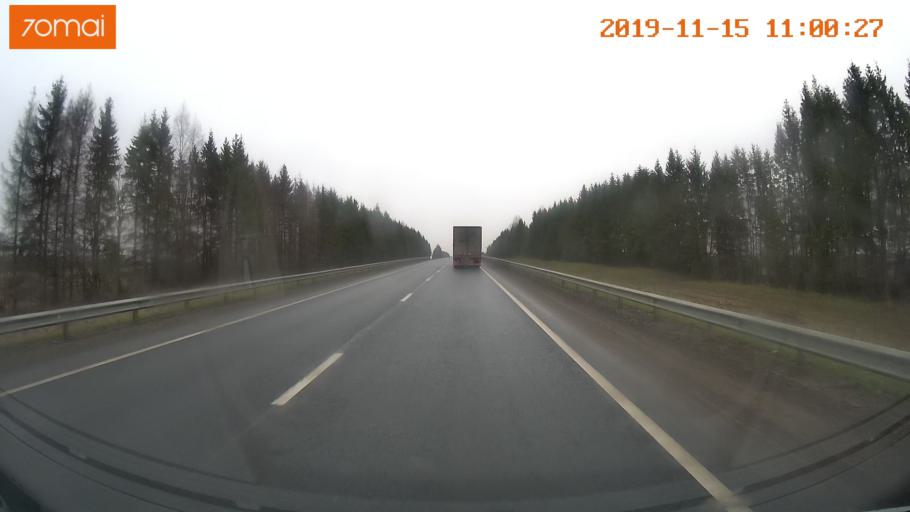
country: RU
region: Vologda
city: Chebsara
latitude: 59.1371
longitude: 38.8996
